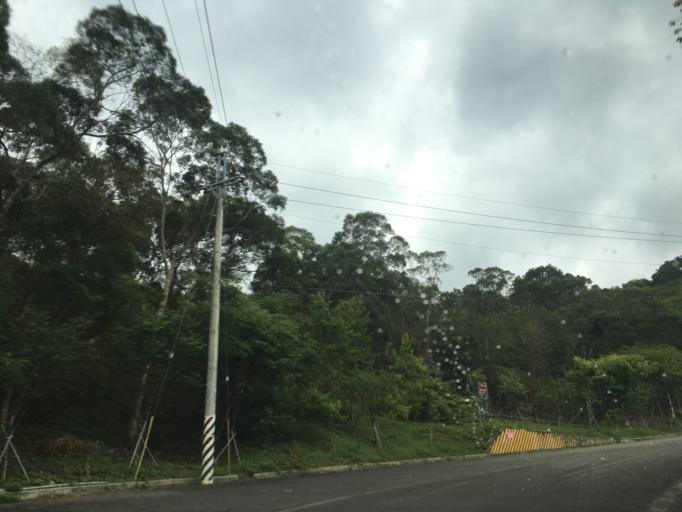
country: TW
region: Taiwan
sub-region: Taichung City
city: Taichung
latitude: 24.0661
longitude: 120.7181
